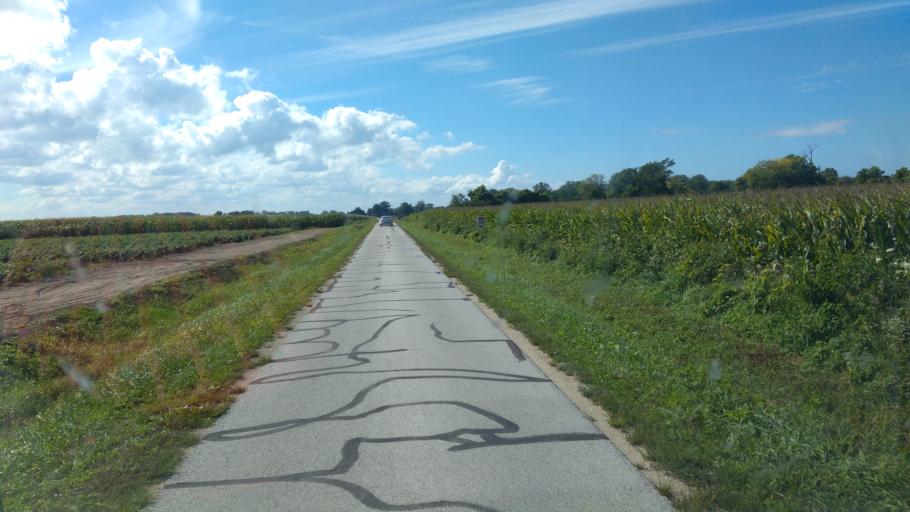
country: US
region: Ohio
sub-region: Ottawa County
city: Port Clinton
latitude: 41.4083
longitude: -82.8749
